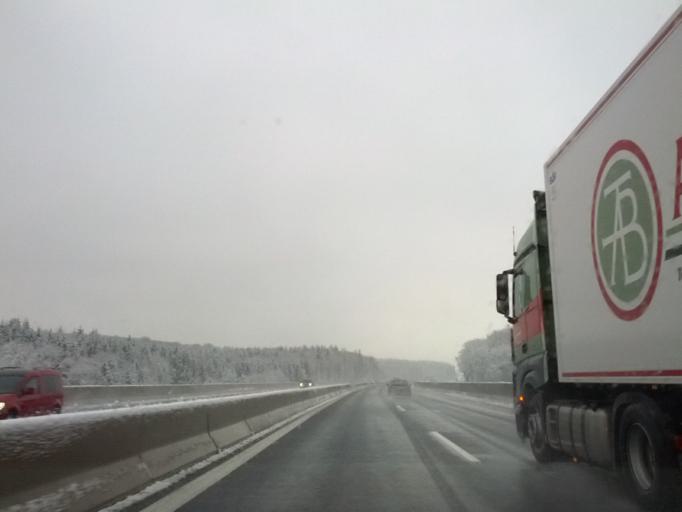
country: DE
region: Bavaria
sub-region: Regierungsbezirk Unterfranken
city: Rannungen
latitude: 50.1634
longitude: 10.1801
